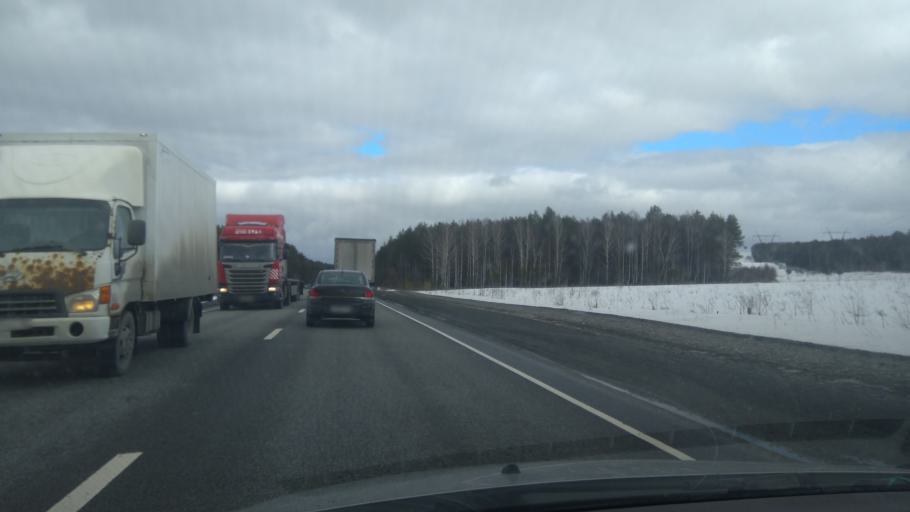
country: RU
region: Sverdlovsk
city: Bisert'
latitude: 56.8250
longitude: 58.7669
